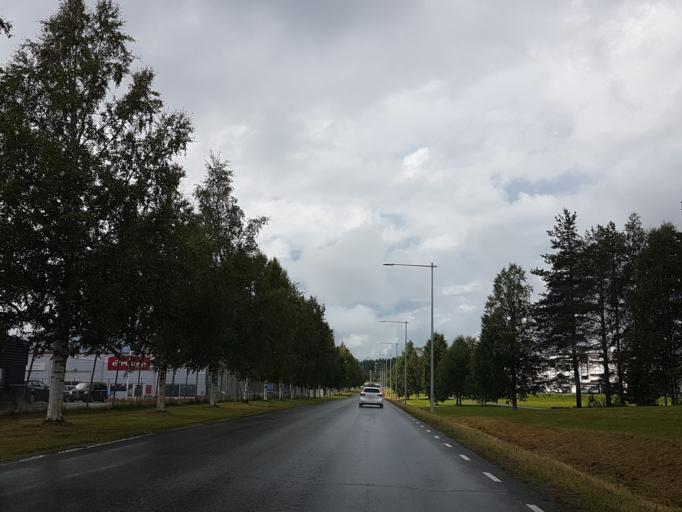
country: SE
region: Vaesterbotten
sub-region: Umea Kommun
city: Ersmark
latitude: 63.8523
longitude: 20.3133
